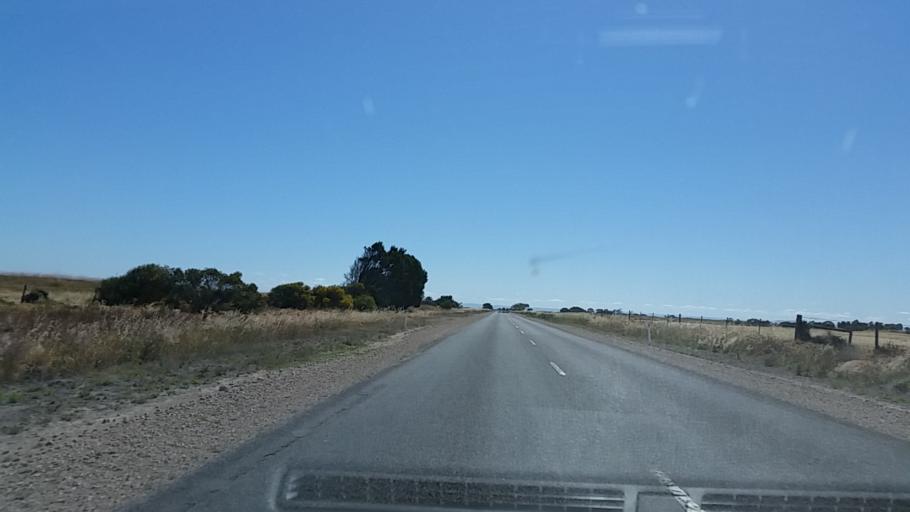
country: AU
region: South Australia
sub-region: Murray Bridge
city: Tailem Bend
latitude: -35.3259
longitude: 139.2629
